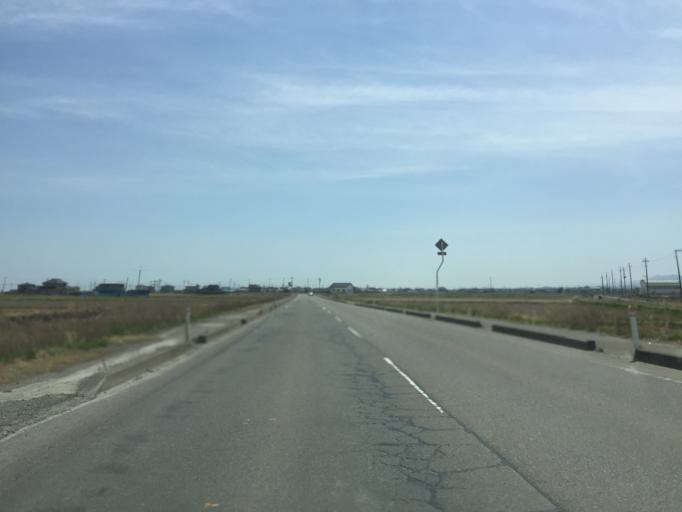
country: JP
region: Miyagi
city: Watari
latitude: 38.0137
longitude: 140.8914
